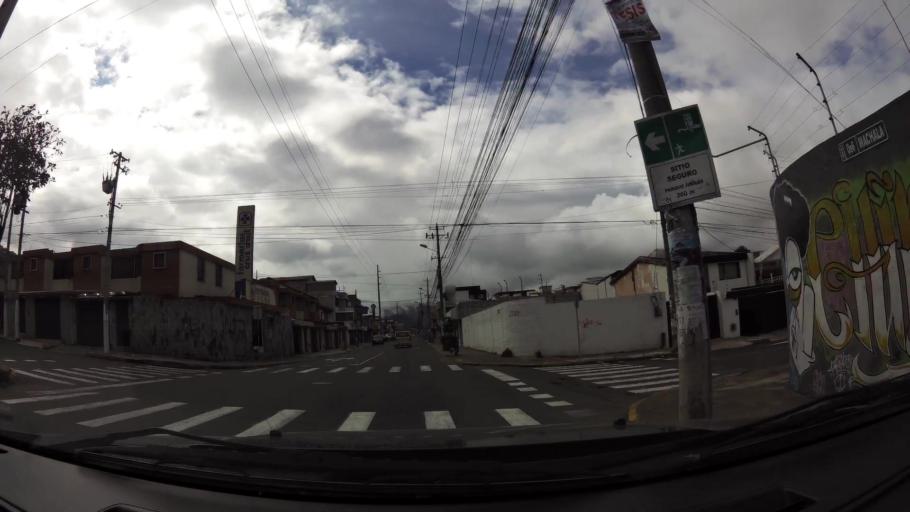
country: EC
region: Pichincha
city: Quito
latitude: -0.1314
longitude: -78.4979
